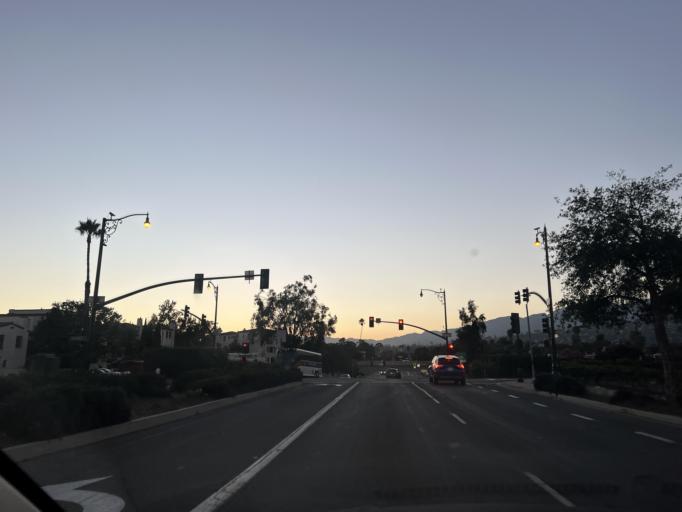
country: US
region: California
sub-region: Santa Barbara County
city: Santa Barbara
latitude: 34.4170
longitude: -119.6881
